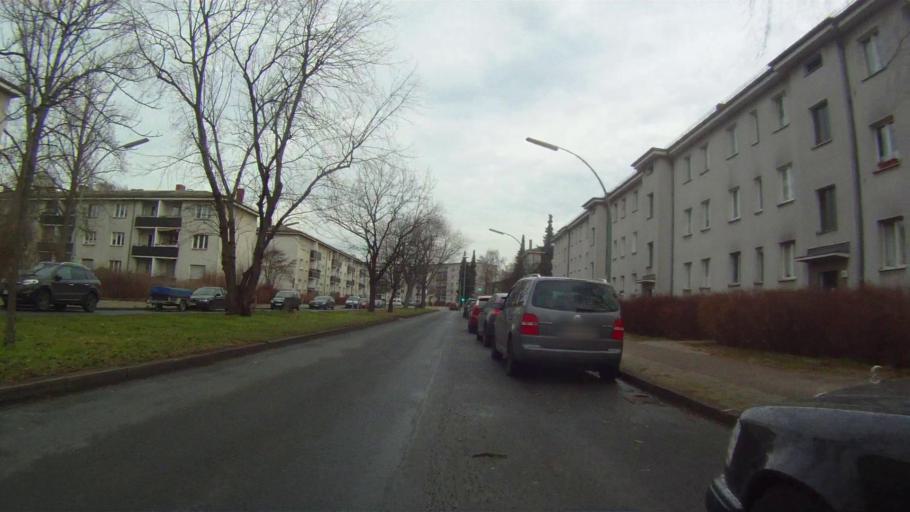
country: DE
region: Berlin
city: Mariendorf
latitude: 52.4270
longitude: 13.4036
